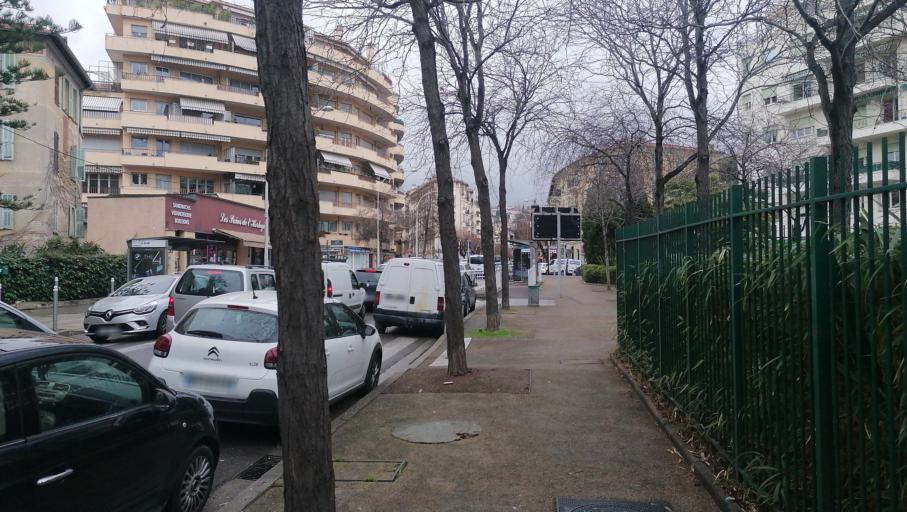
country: FR
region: Provence-Alpes-Cote d'Azur
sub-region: Departement des Alpes-Maritimes
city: Nice
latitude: 43.7187
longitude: 7.2524
